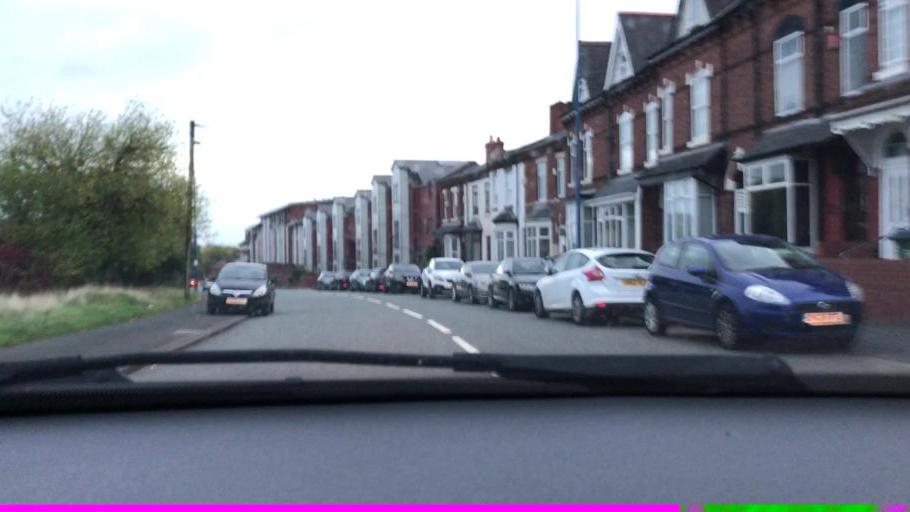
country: GB
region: England
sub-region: Sandwell
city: Smethwick
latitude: 52.4866
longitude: -1.9663
